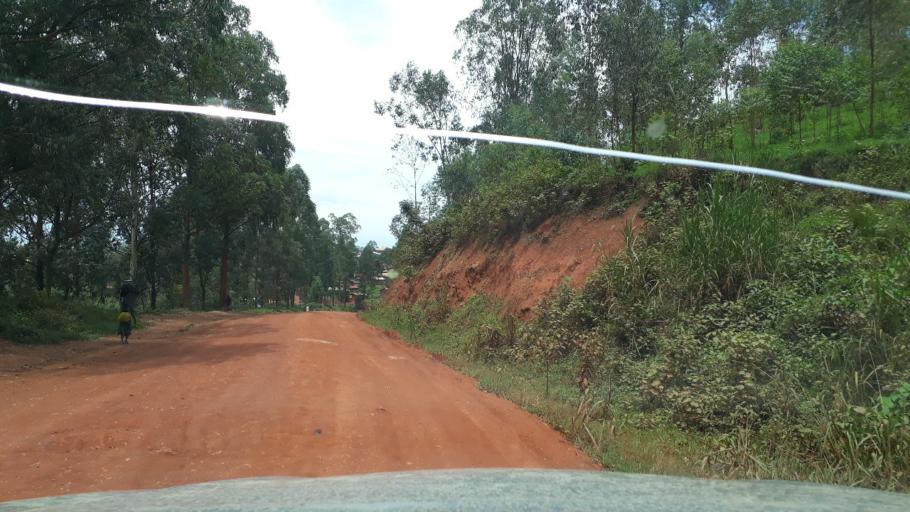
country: CD
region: Eastern Province
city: Bunia
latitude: 1.7276
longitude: 30.3024
